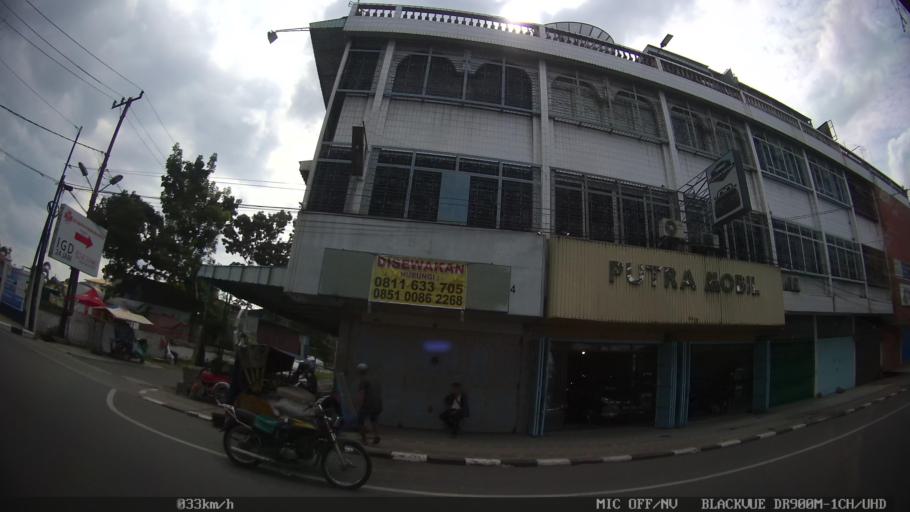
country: ID
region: North Sumatra
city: Medan
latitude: 3.5763
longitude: 98.6846
